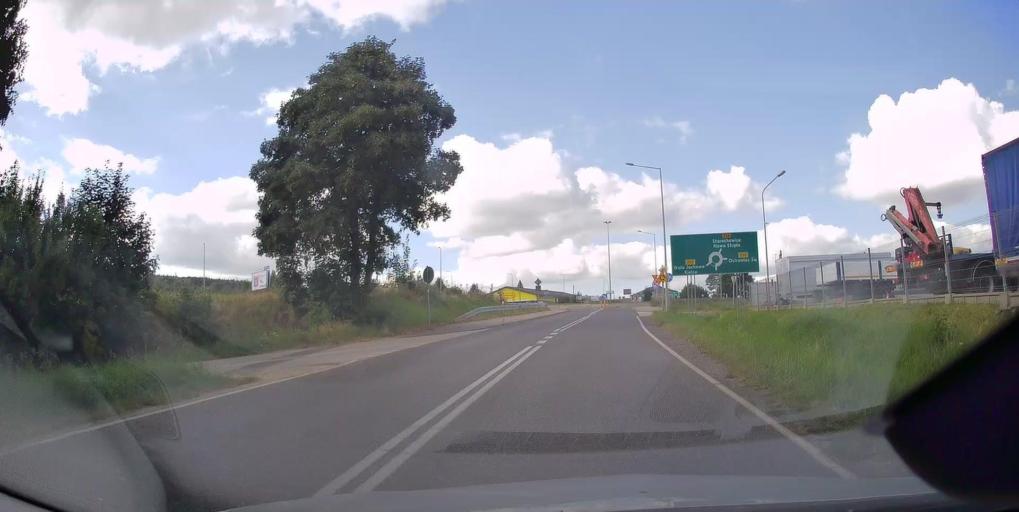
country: PL
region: Swietokrzyskie
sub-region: Powiat kielecki
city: Nowa Slupia
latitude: 50.8498
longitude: 21.0843
